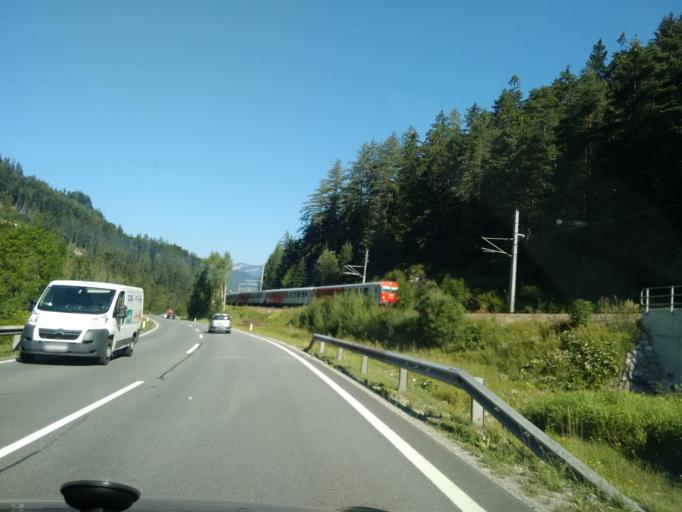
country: AT
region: Styria
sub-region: Politischer Bezirk Liezen
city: Bad Aussee
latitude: 47.5890
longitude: 13.7996
